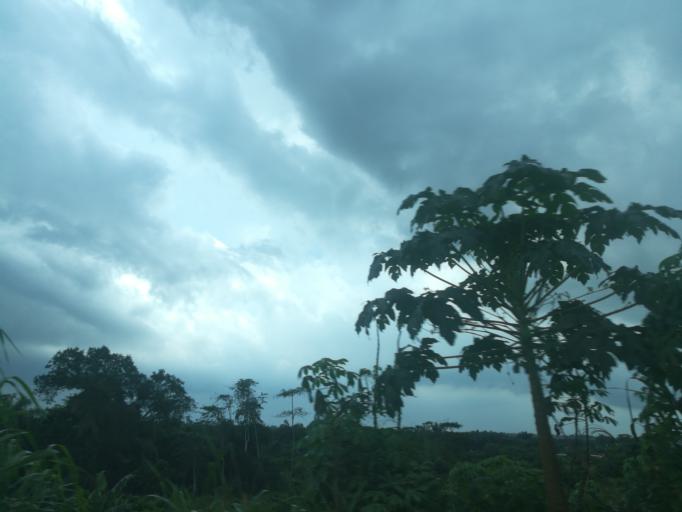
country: NG
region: Lagos
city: Ikorodu
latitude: 6.6607
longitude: 3.5892
